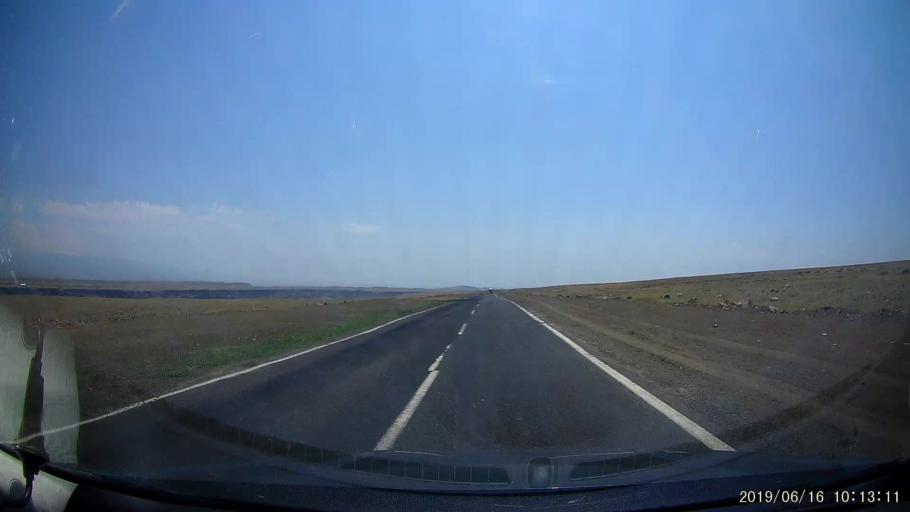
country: TR
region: Igdir
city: Tuzluca
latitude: 40.1935
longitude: 43.6374
